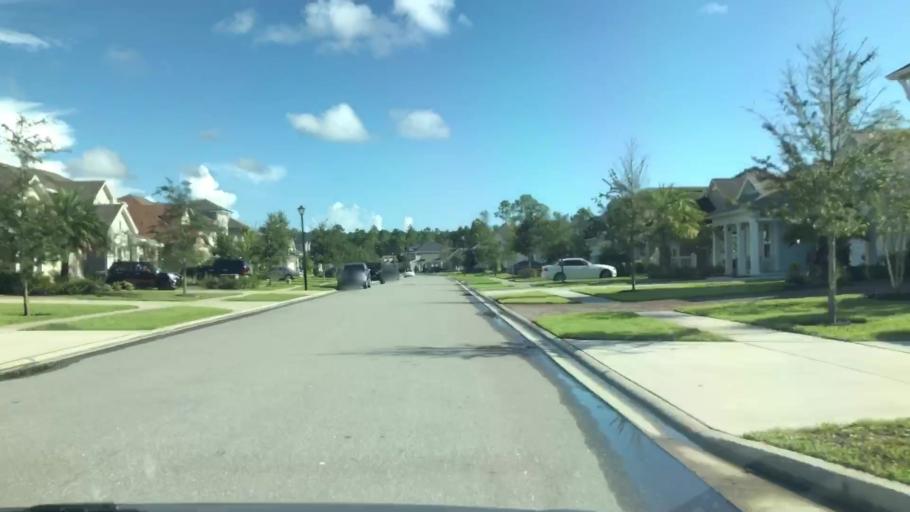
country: US
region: Florida
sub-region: Saint Johns County
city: Palm Valley
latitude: 30.1259
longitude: -81.4086
